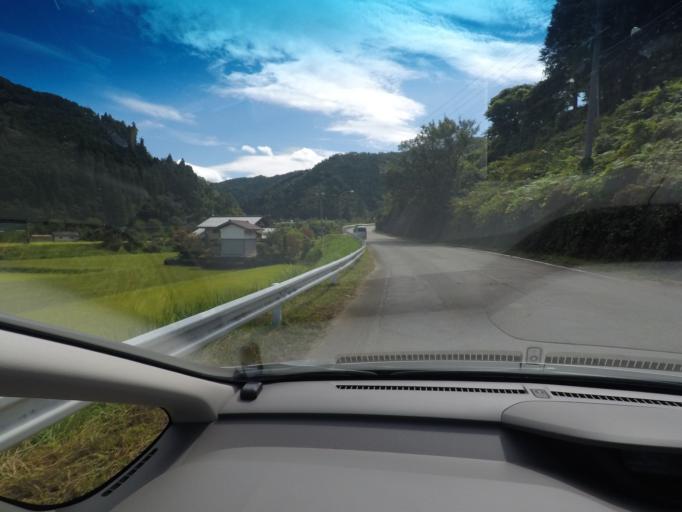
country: JP
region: Gifu
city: Takayama
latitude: 36.1338
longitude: 137.3133
